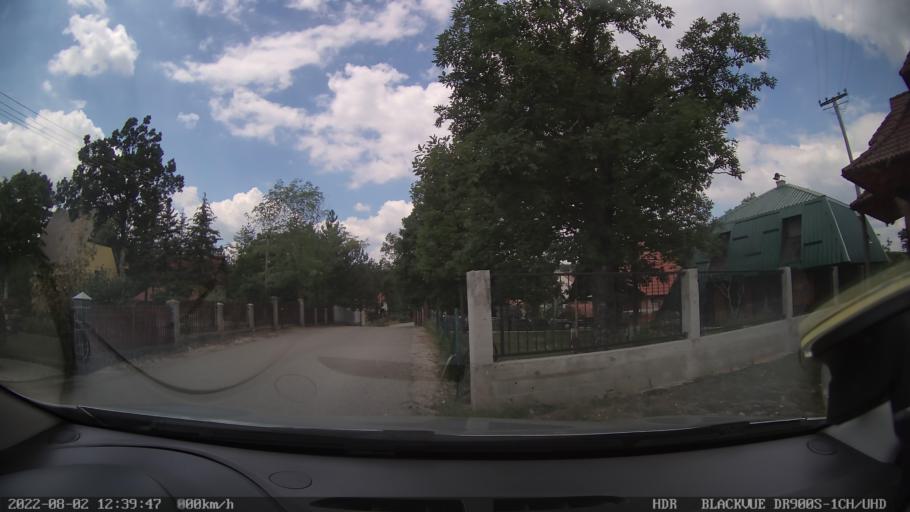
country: RS
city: Zlatibor
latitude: 43.7079
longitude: 19.7203
